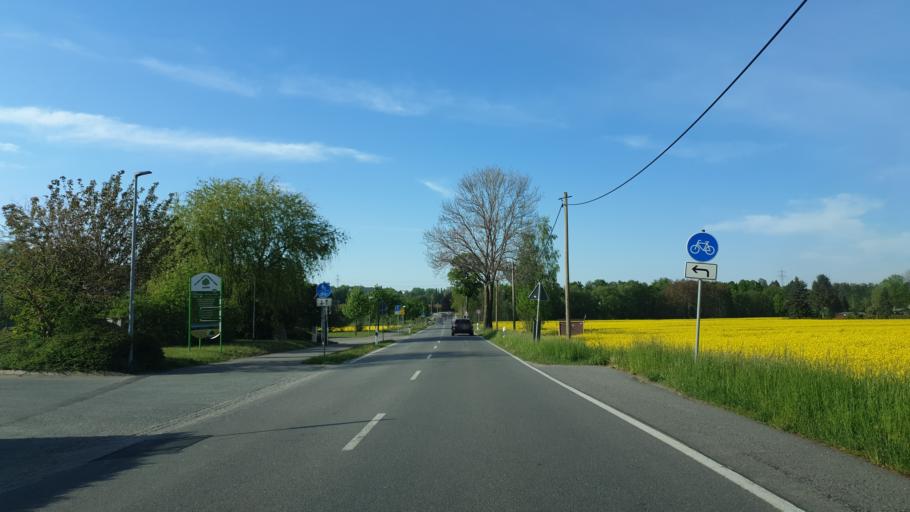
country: DE
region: Saxony
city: Neukirchen
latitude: 50.7662
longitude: 12.8750
